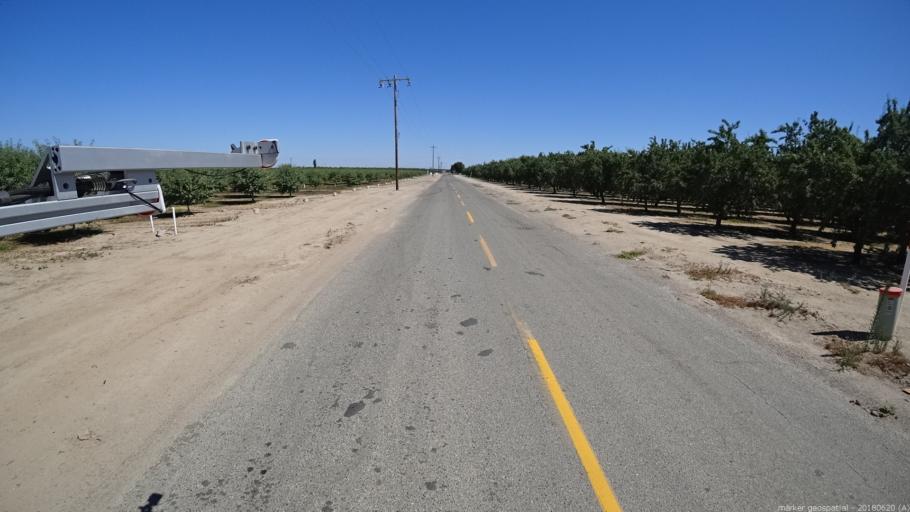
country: US
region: California
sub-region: Madera County
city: Parkwood
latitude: 36.8999
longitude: -120.0015
